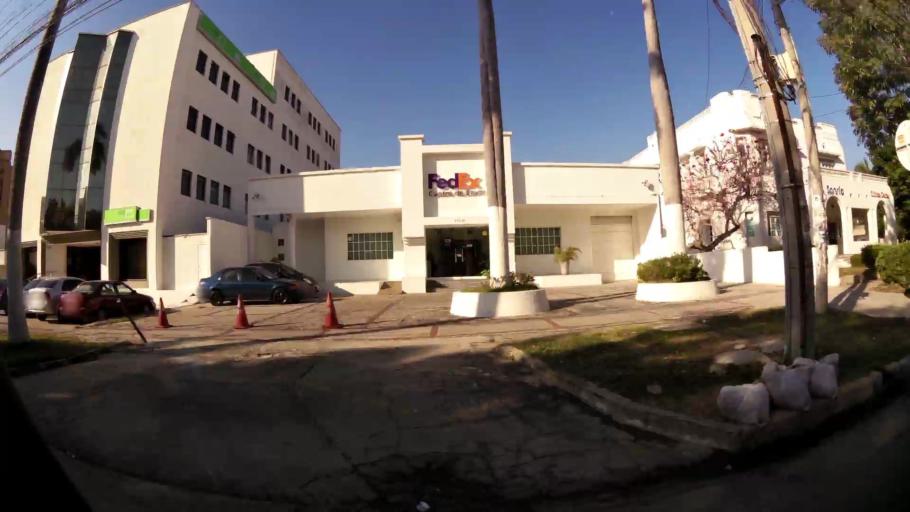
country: CO
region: Atlantico
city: Barranquilla
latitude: 10.9989
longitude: -74.8042
